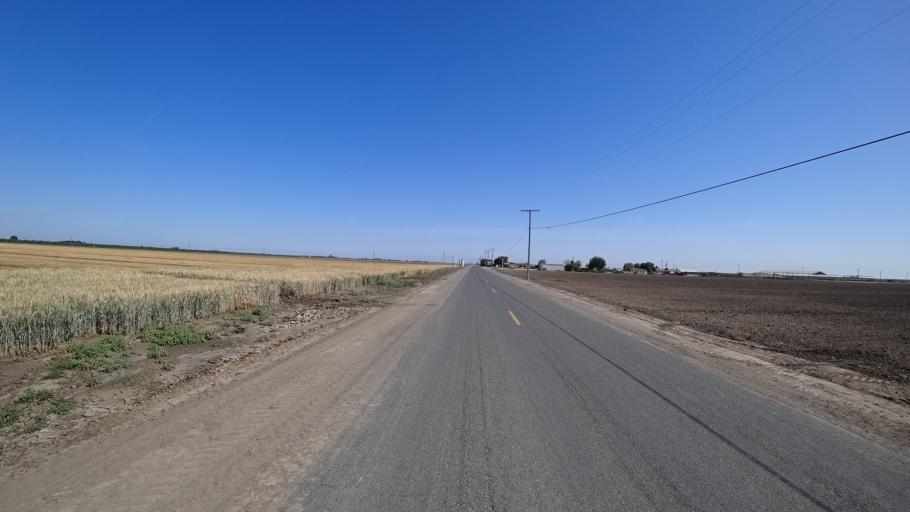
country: US
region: California
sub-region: Kings County
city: Home Garden
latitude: 36.2524
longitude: -119.5474
